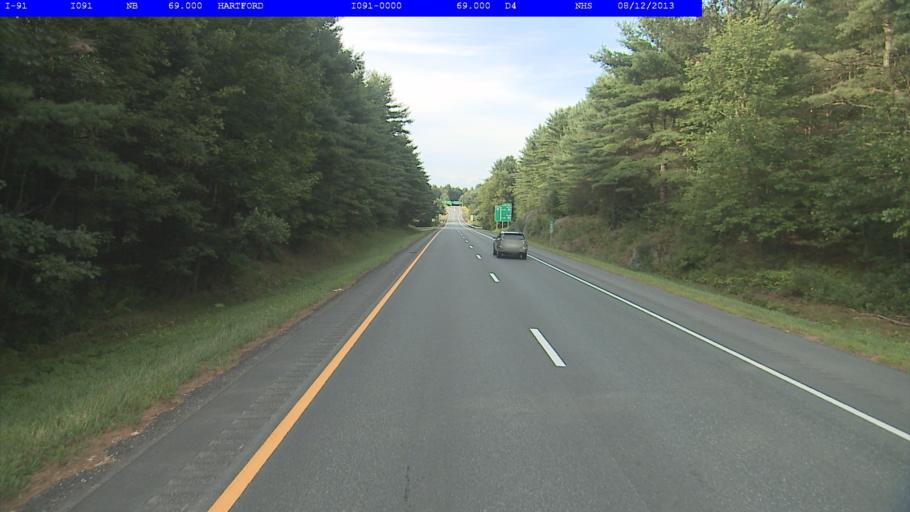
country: US
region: Vermont
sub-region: Windsor County
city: White River Junction
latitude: 43.6285
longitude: -72.3421
